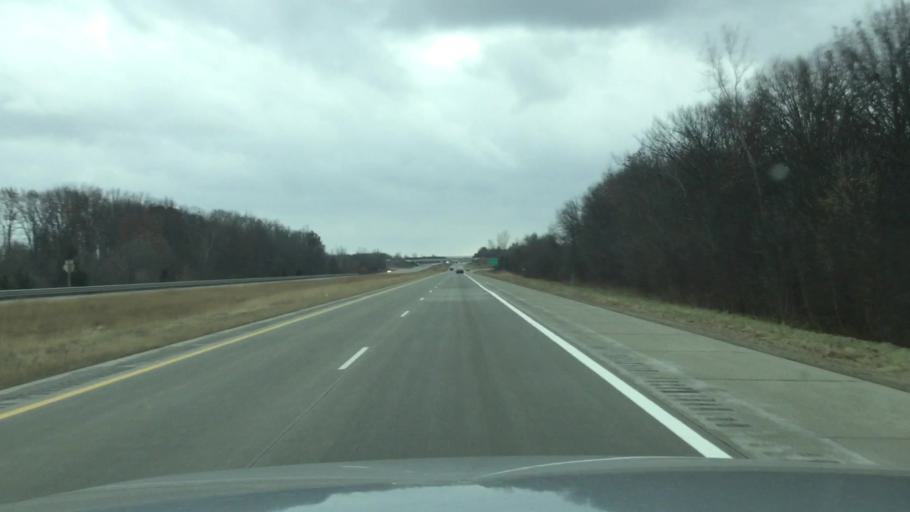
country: US
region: Michigan
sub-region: Genesee County
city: Grand Blanc
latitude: 42.9535
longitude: -83.6824
